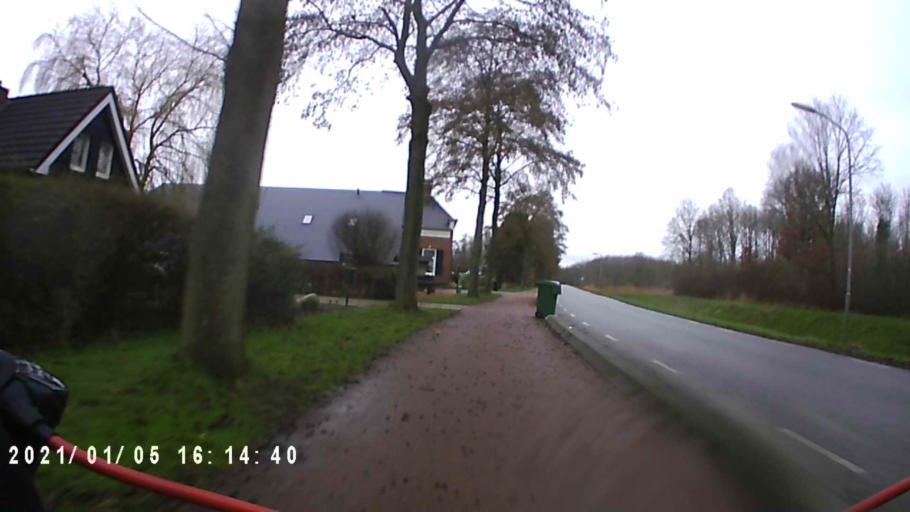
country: NL
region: Groningen
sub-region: Gemeente  Oldambt
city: Winschoten
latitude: 53.1935
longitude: 7.0634
